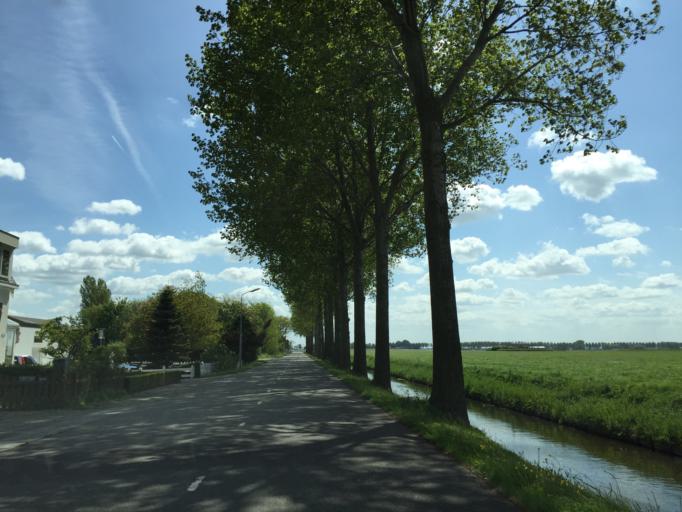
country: NL
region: North Holland
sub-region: Gemeente Haarlemmermeer
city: Hoofddorp
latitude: 52.3368
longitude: 4.7020
